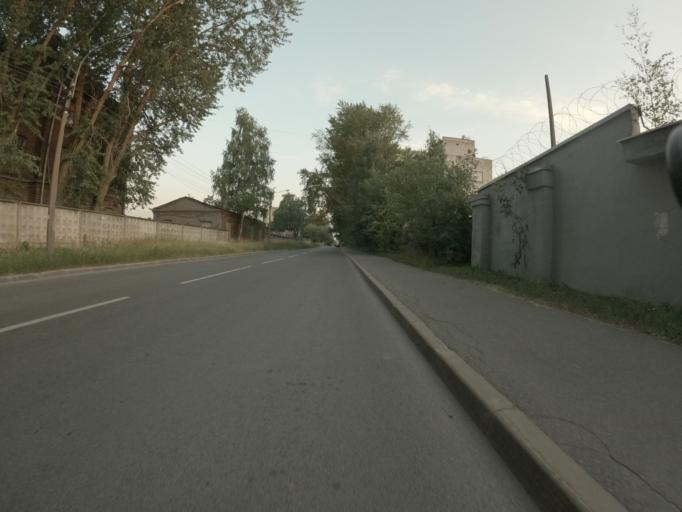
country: RU
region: St.-Petersburg
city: Kupchino
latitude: 59.8922
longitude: 30.3379
